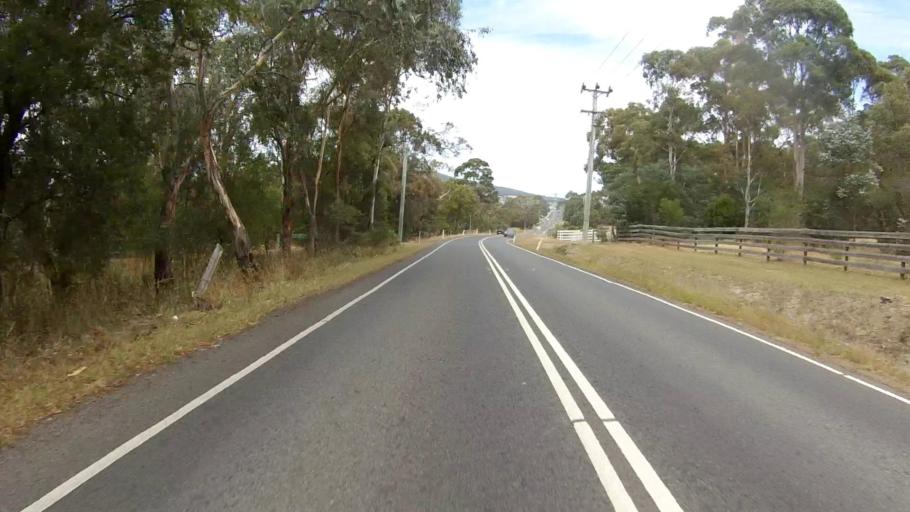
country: AU
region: Tasmania
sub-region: Clarence
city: Lauderdale
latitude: -42.8991
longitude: 147.4801
